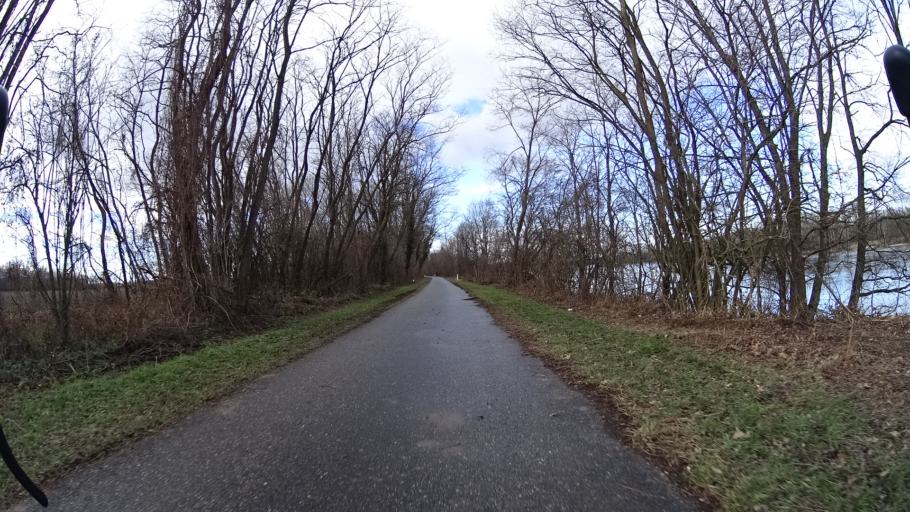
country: AT
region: Lower Austria
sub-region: Politischer Bezirk Tulln
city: Atzenbrugg
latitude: 48.3507
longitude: 15.9001
